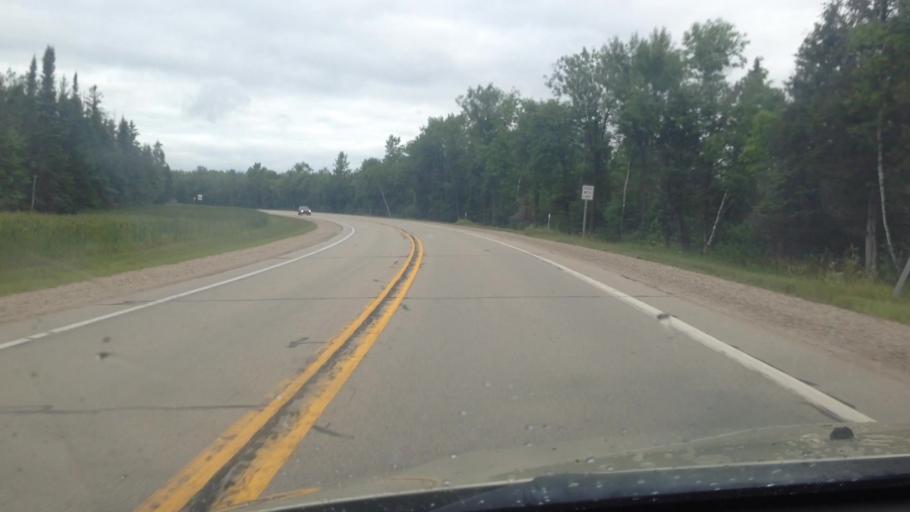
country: US
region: Michigan
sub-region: Menominee County
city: Menominee
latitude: 45.4191
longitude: -87.3465
